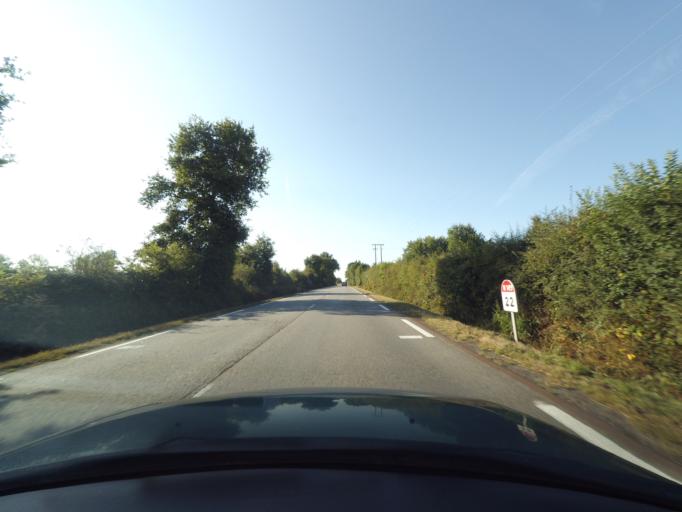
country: FR
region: Poitou-Charentes
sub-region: Departement des Deux-Sevres
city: Viennay
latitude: 46.6941
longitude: -0.2754
